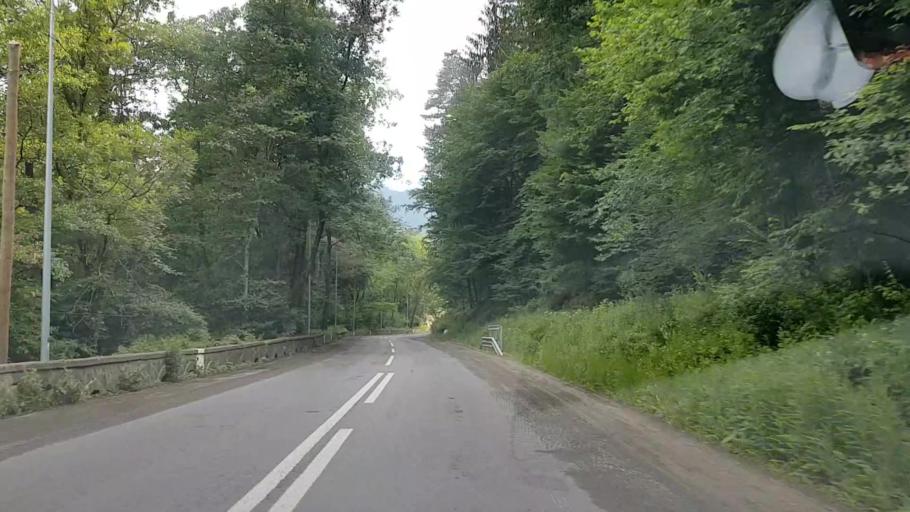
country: RO
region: Neamt
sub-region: Comuna Bicaz
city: Dodeni
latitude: 46.9316
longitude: 26.0964
